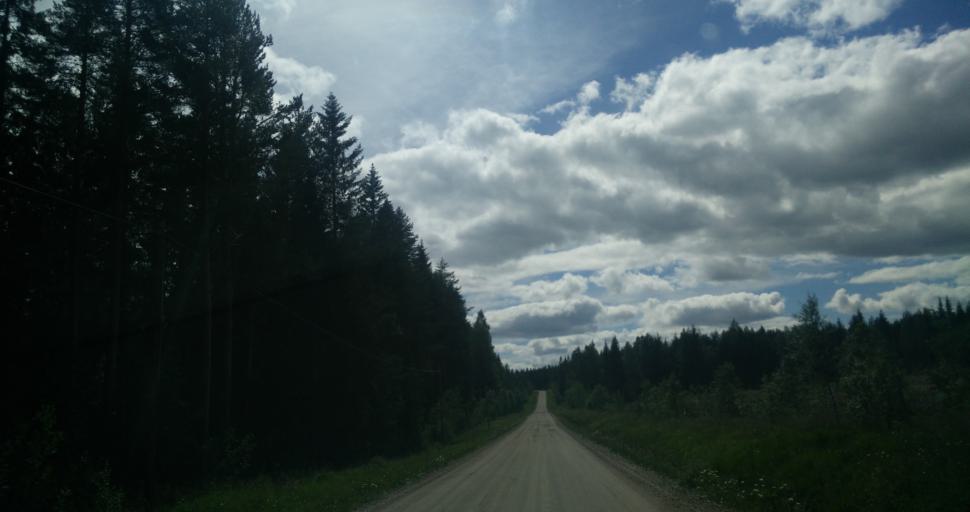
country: SE
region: Vaesternorrland
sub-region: Sundsvalls Kommun
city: Vi
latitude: 62.1424
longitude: 17.1337
